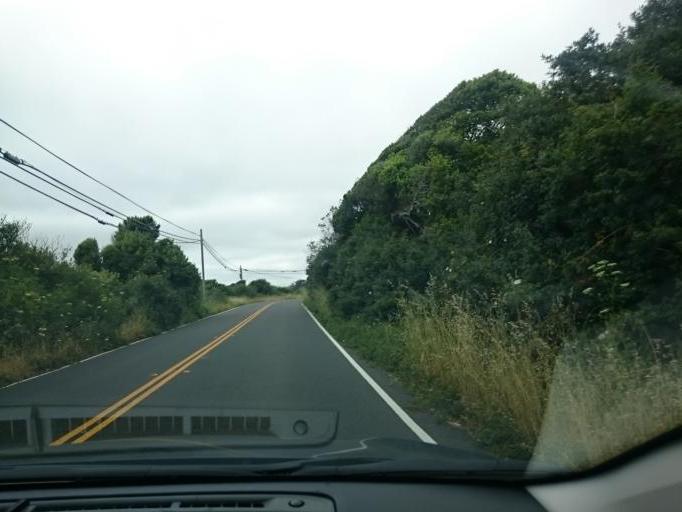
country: US
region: California
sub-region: Marin County
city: Inverness
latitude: 38.1014
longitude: -122.8367
